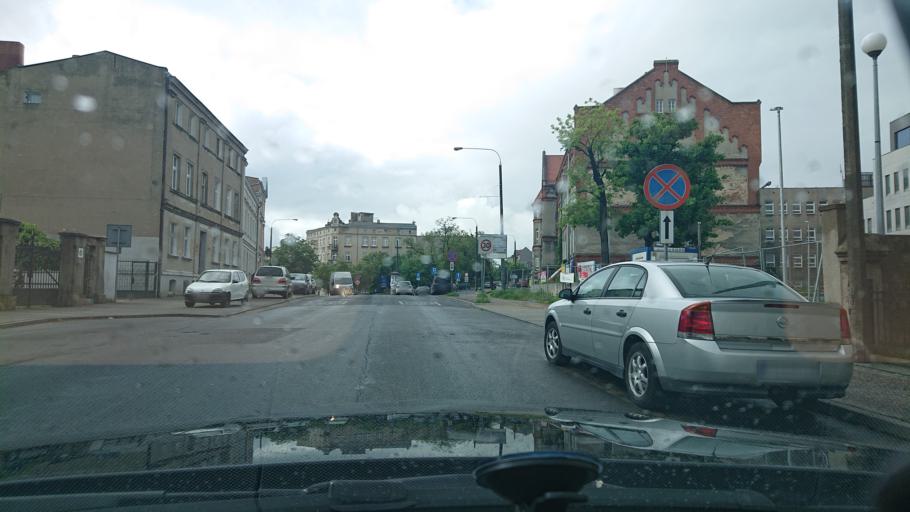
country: PL
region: Greater Poland Voivodeship
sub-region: Powiat gnieznienski
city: Gniezno
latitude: 52.5415
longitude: 17.6005
